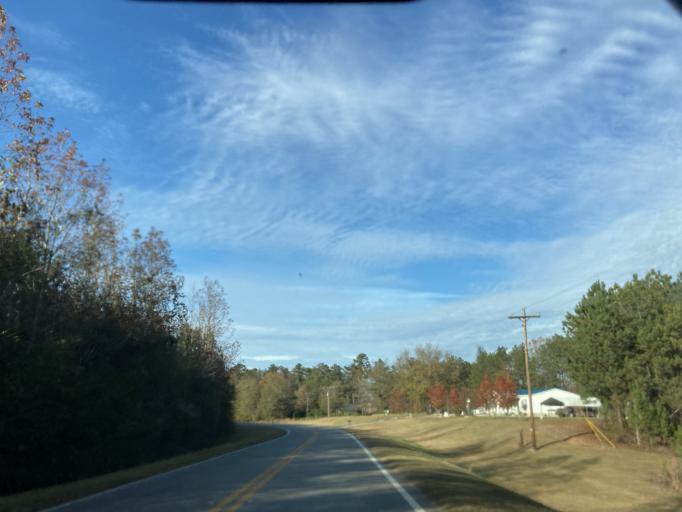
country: US
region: Georgia
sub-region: Jones County
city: Gray
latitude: 32.8834
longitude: -83.4929
